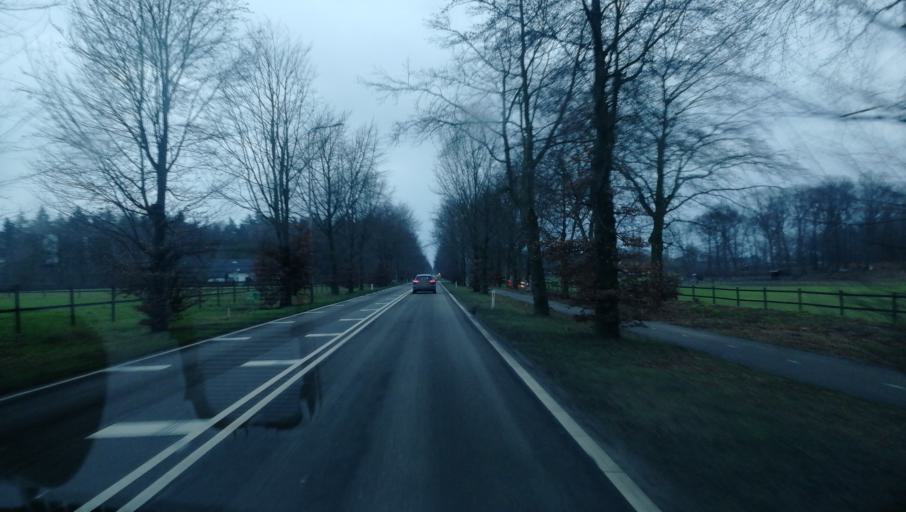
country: NL
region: Limburg
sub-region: Gemeente Beesel
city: Reuver
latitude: 51.3241
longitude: 6.0833
